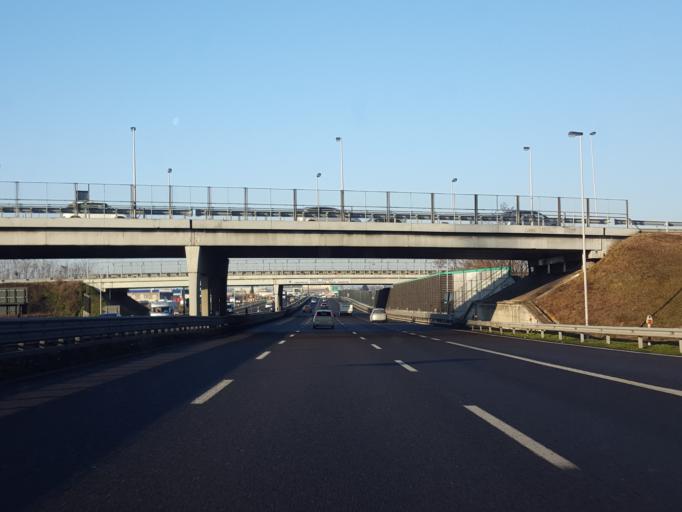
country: IT
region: Veneto
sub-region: Provincia di Verona
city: Soave
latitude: 45.4096
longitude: 11.2496
